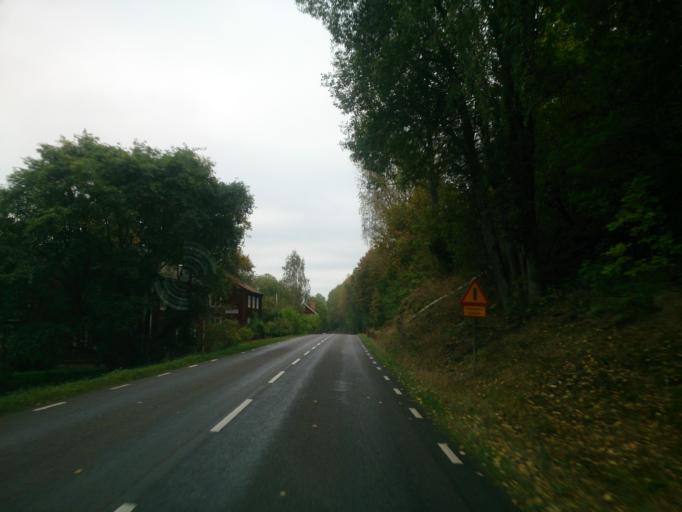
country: SE
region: OEstergoetland
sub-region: Atvidabergs Kommun
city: Atvidaberg
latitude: 58.1821
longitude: 16.1012
